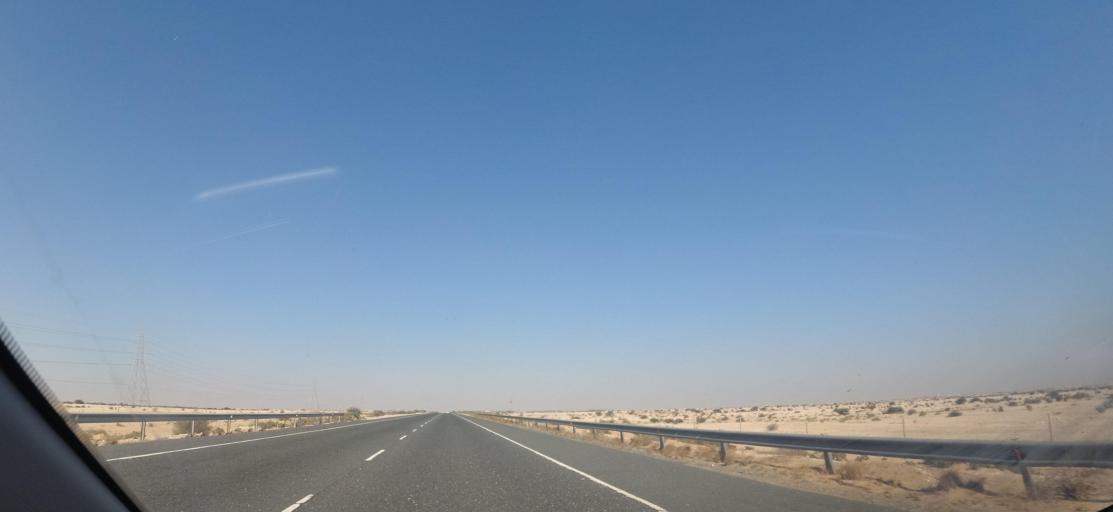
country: QA
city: Al Jumayliyah
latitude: 25.5882
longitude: 51.0623
